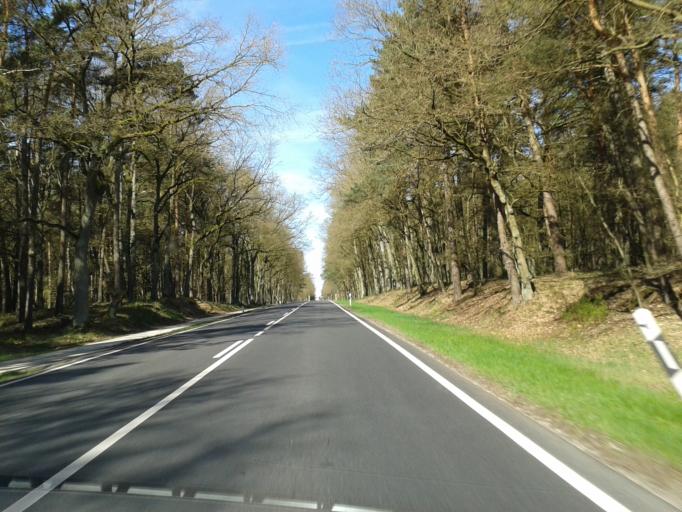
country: DE
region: Lower Saxony
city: Schnega
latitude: 52.9246
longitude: 10.8517
